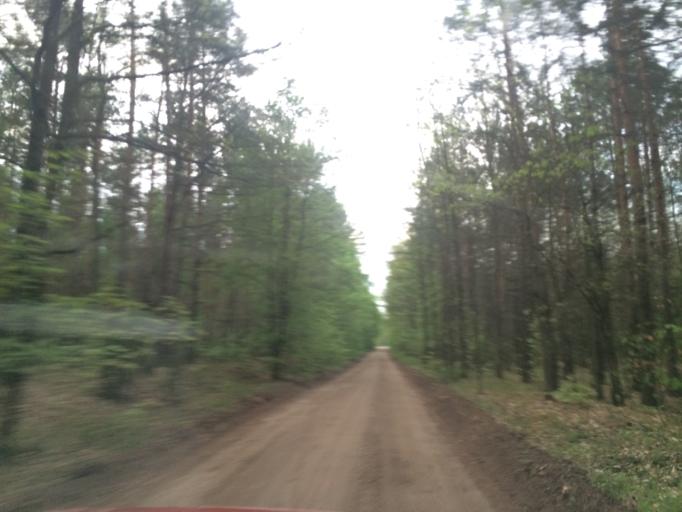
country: PL
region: Warmian-Masurian Voivodeship
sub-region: Powiat nowomiejski
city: Kurzetnik
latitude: 53.3679
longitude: 19.5206
